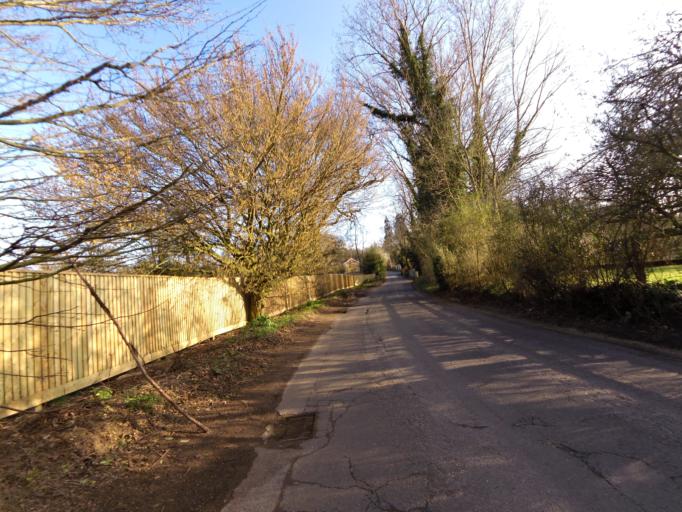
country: GB
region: England
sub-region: Suffolk
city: Kesgrave
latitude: 52.0828
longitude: 1.2537
